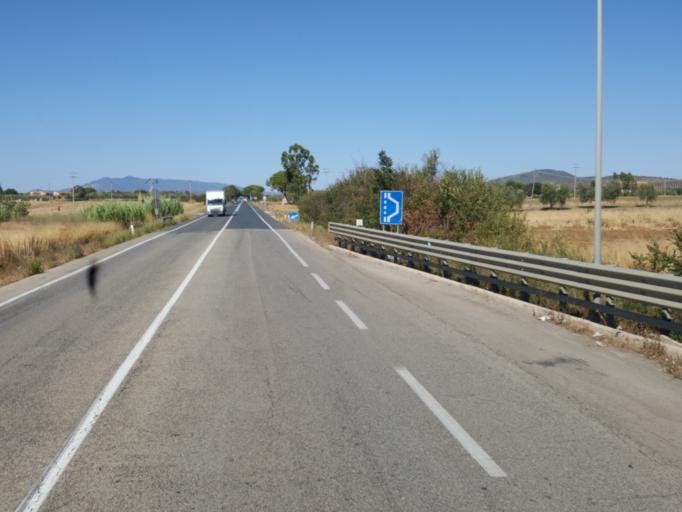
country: IT
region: Tuscany
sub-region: Provincia di Grosseto
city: Capalbio
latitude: 42.4146
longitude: 11.4246
